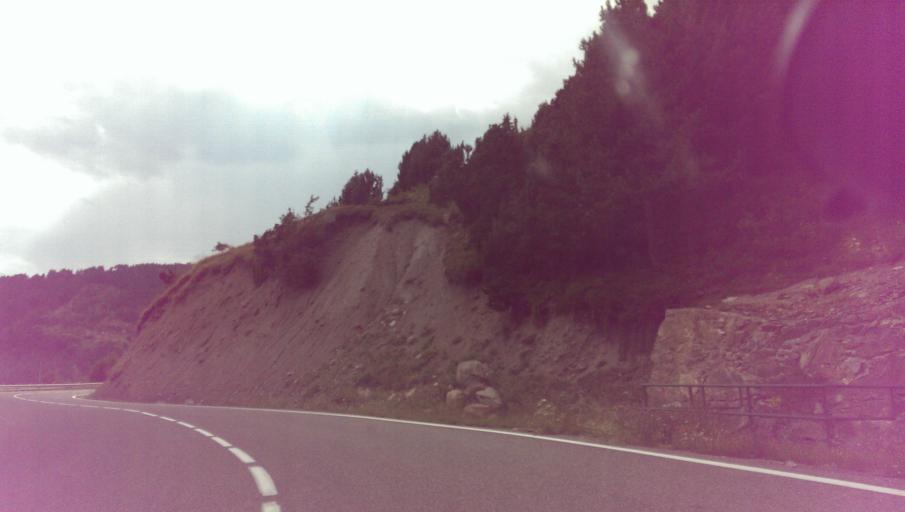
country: AD
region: Canillo
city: Canillo
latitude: 42.5726
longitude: 1.5956
